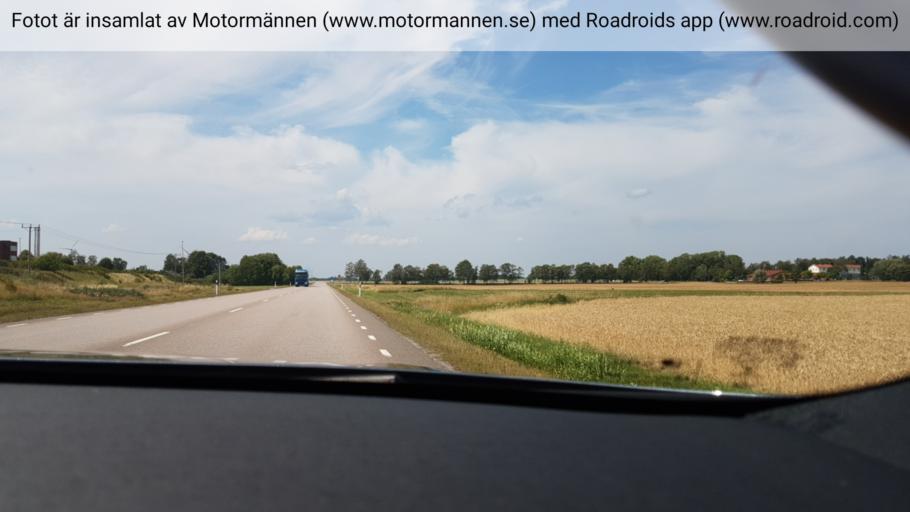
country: SE
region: Vaestra Goetaland
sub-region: Skara Kommun
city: Skara
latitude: 58.3928
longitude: 13.4343
